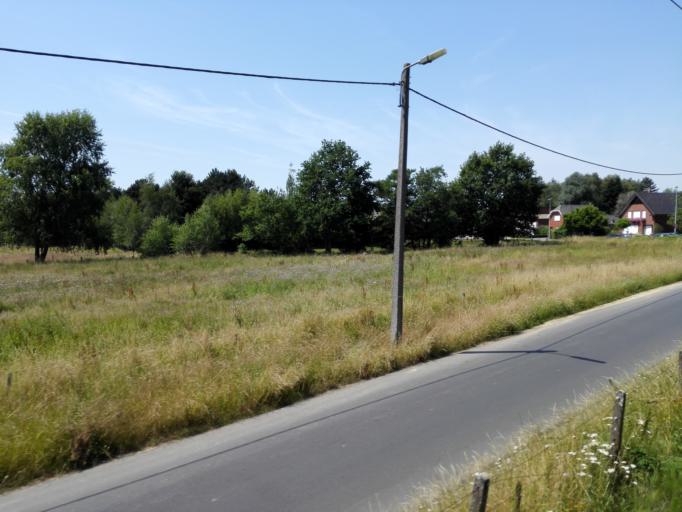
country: BE
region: Flanders
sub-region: Provincie Antwerpen
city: Heist-op-den-Berg
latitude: 51.0512
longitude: 4.7489
